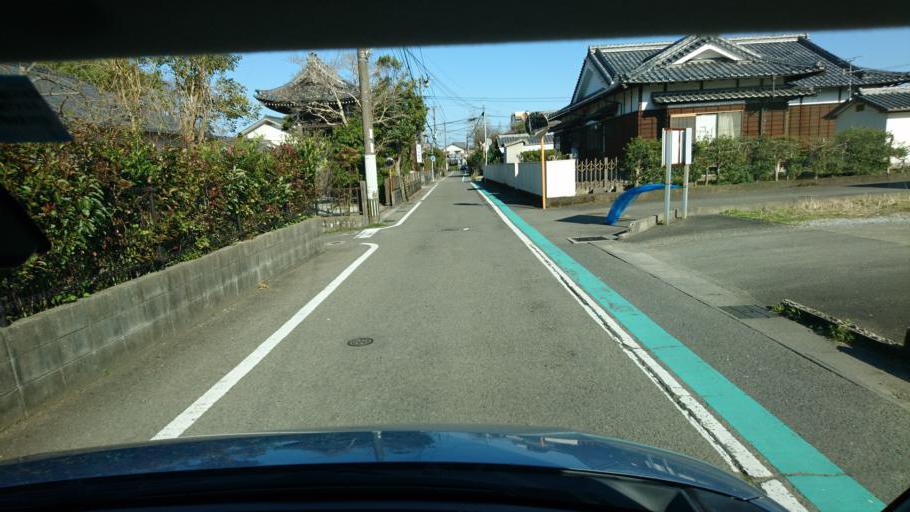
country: JP
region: Miyazaki
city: Miyazaki-shi
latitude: 31.8327
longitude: 131.4360
